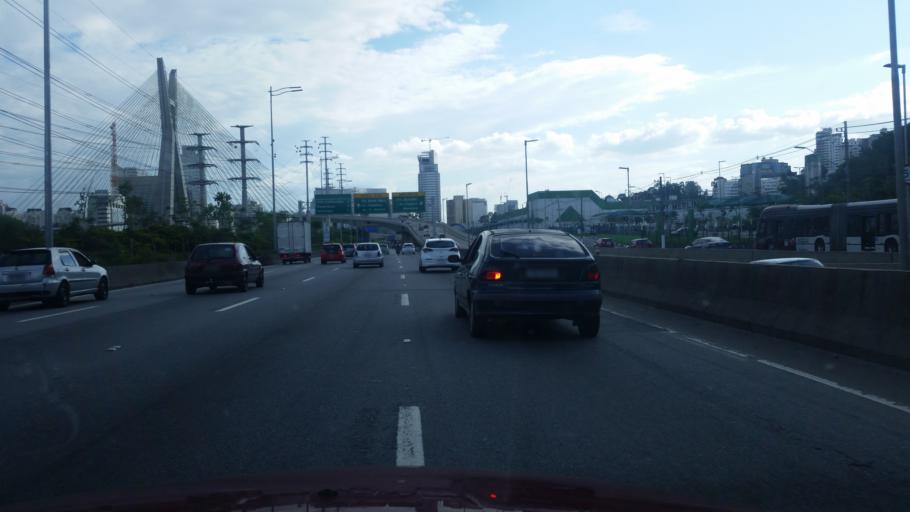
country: BR
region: Sao Paulo
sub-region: Sao Paulo
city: Sao Paulo
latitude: -23.6075
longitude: -46.6995
